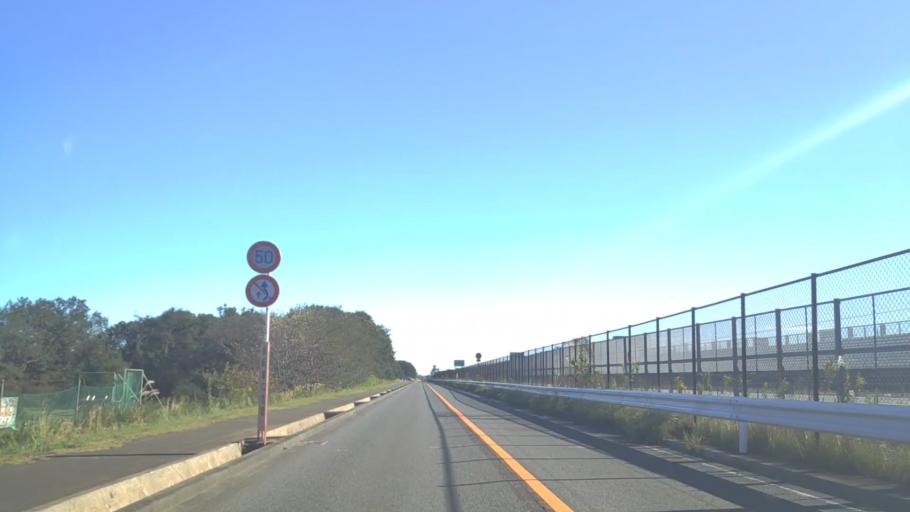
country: JP
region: Kanagawa
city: Zama
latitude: 35.4762
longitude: 139.3746
